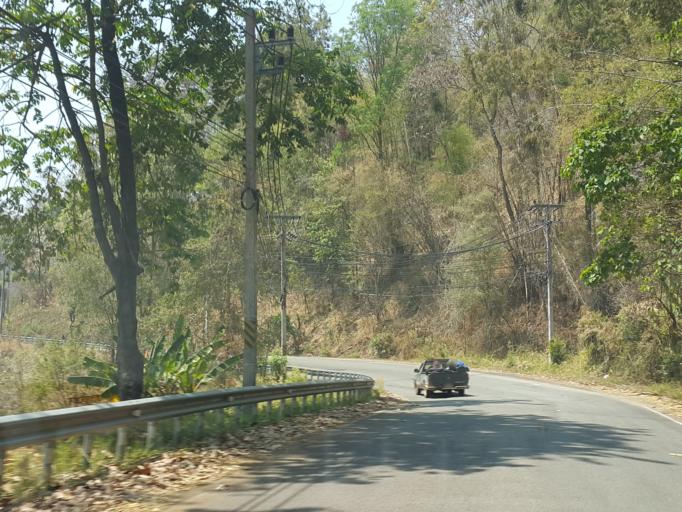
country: TH
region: Chiang Mai
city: Samoeng
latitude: 18.8650
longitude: 98.7822
